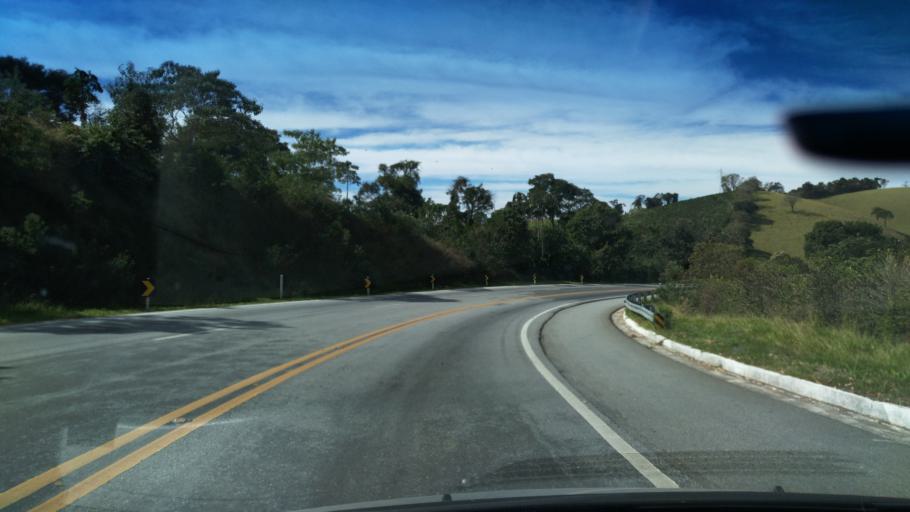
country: BR
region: Minas Gerais
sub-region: Borda Da Mata
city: Borda da Mata
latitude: -22.1350
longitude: -46.1590
